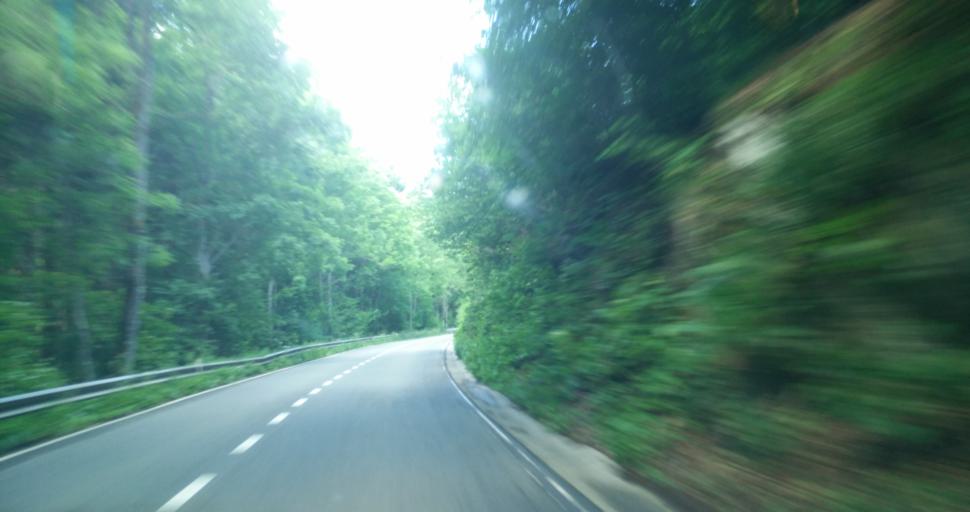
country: BE
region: Wallonia
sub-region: Province du Luxembourg
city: La Roche-en-Ardenne
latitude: 50.1795
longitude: 5.6449
